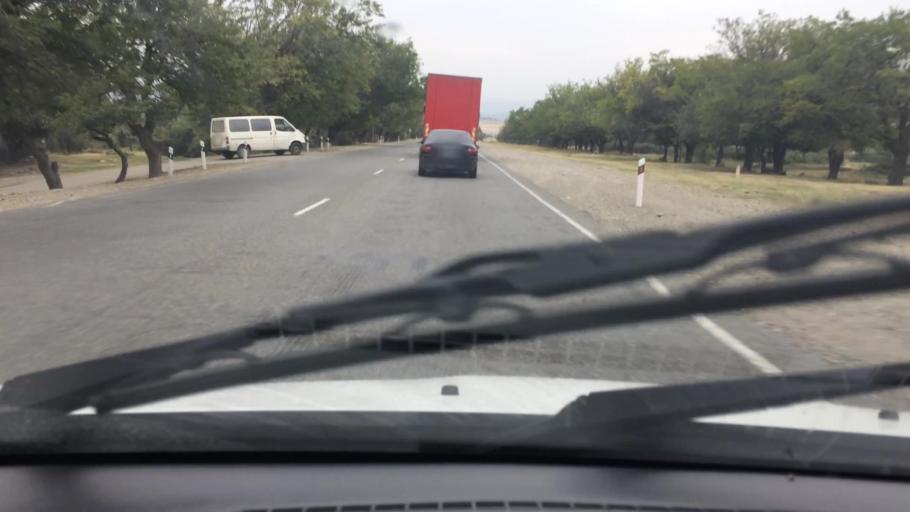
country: GE
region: T'bilisi
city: Tbilisi
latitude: 41.6420
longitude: 44.8592
